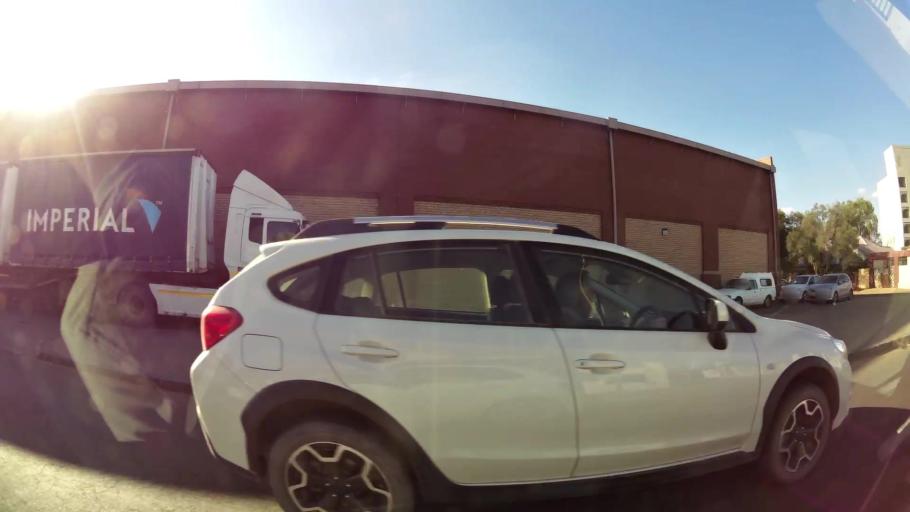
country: ZA
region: Northern Cape
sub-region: Frances Baard District Municipality
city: Kimberley
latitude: -28.7460
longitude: 24.7626
